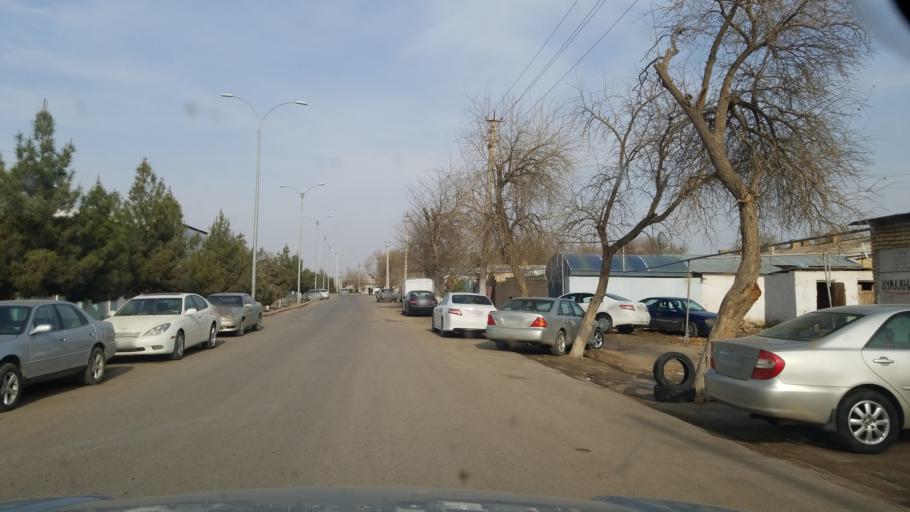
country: TM
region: Mary
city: Bayramaly
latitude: 37.6225
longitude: 62.1621
